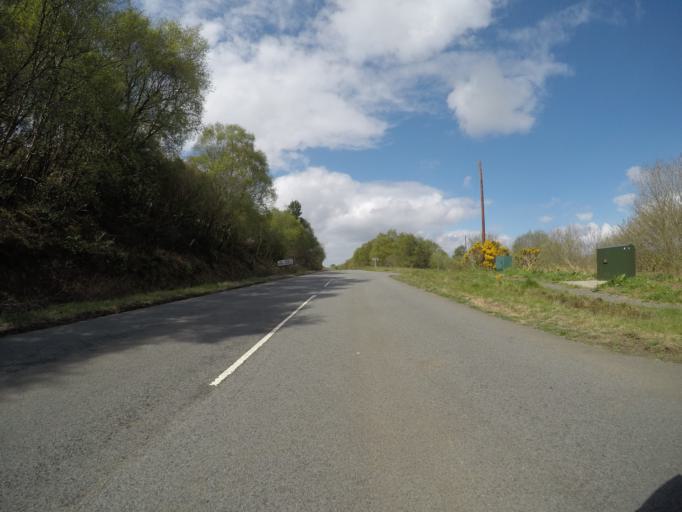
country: GB
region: Scotland
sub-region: Highland
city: Isle of Skye
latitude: 57.4605
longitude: -6.3296
